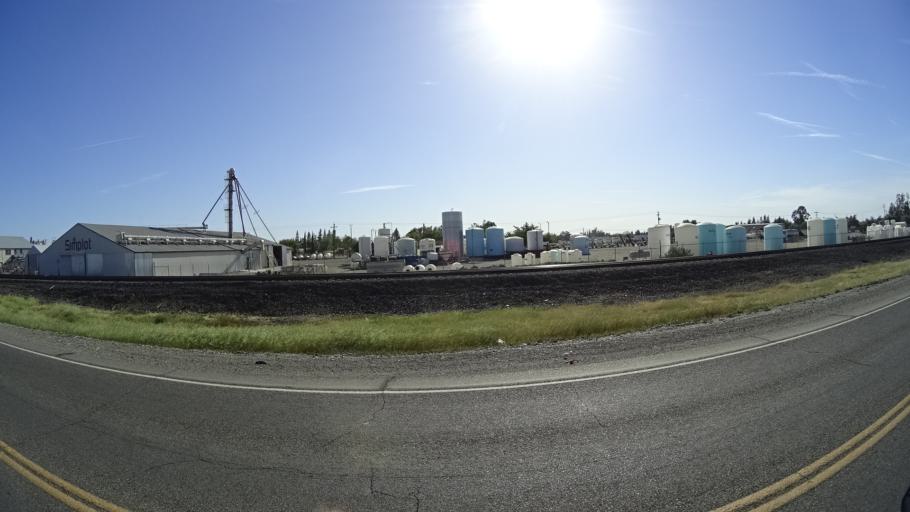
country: US
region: California
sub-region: Glenn County
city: Orland
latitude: 39.7349
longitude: -122.1970
